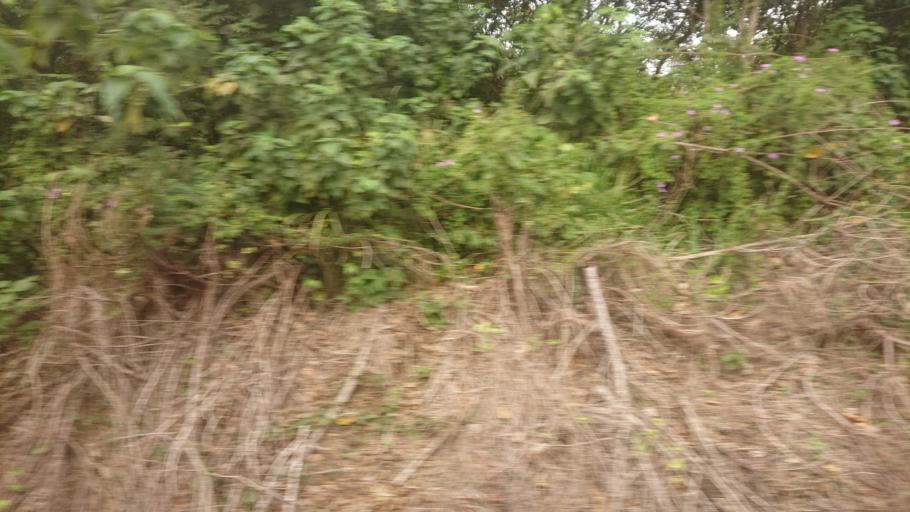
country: TW
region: Taiwan
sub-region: Yunlin
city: Douliu
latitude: 23.7590
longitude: 120.6137
